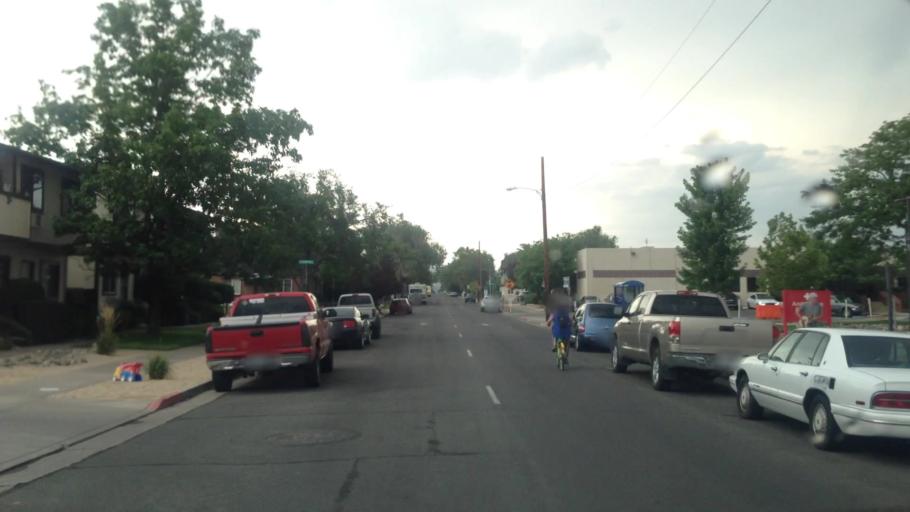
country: US
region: Nevada
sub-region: Washoe County
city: Reno
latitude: 39.5157
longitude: -119.8005
